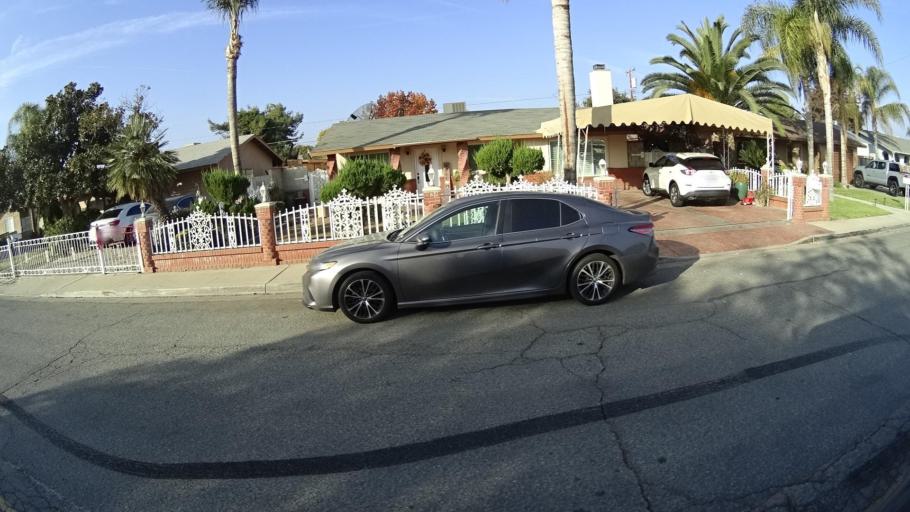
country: US
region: California
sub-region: Kern County
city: McFarland
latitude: 35.6768
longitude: -119.2186
